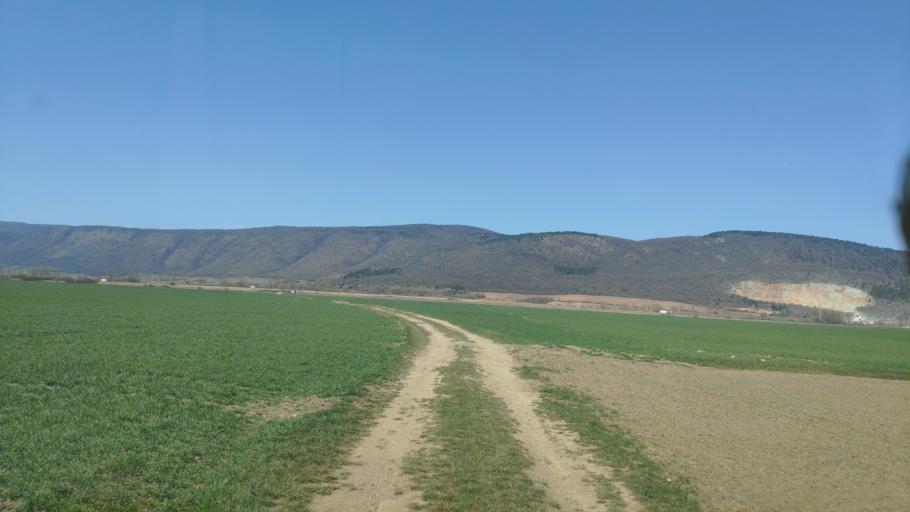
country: SK
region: Kosicky
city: Moldava nad Bodvou
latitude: 48.6006
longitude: 20.9311
